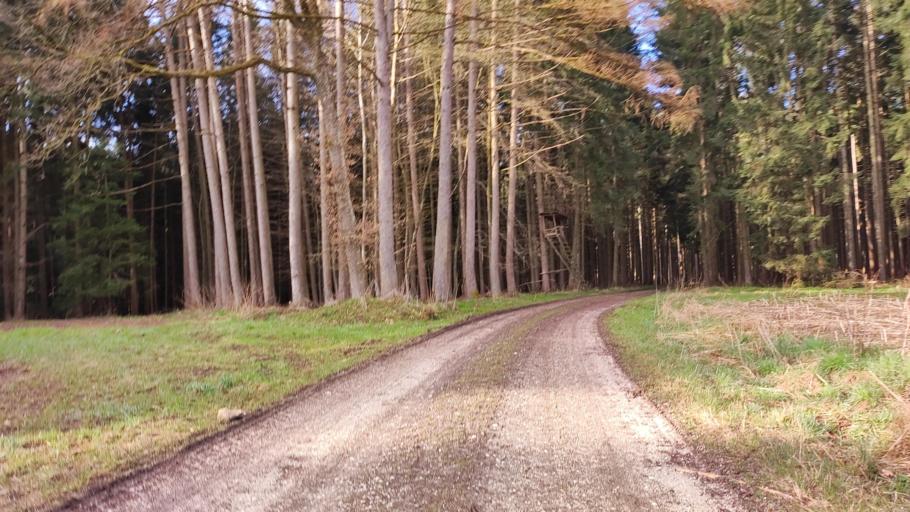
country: DE
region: Bavaria
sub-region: Swabia
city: Altenmunster
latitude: 48.4353
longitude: 10.5740
